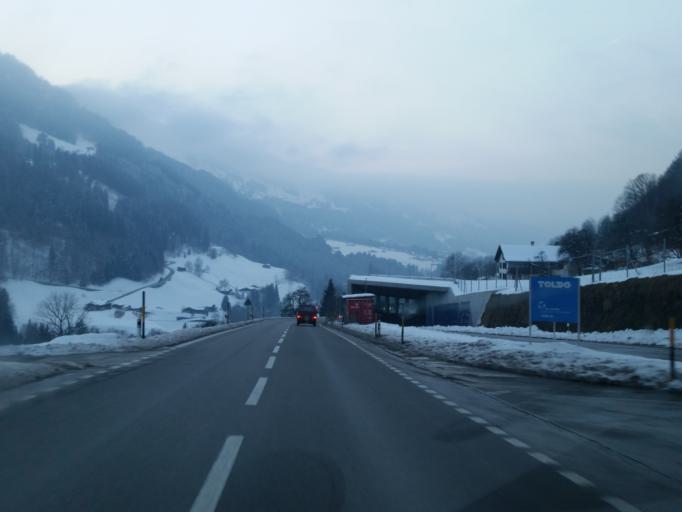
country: CH
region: Grisons
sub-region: Praettigau/Davos District
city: Luzein
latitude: 46.9140
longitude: 9.7920
